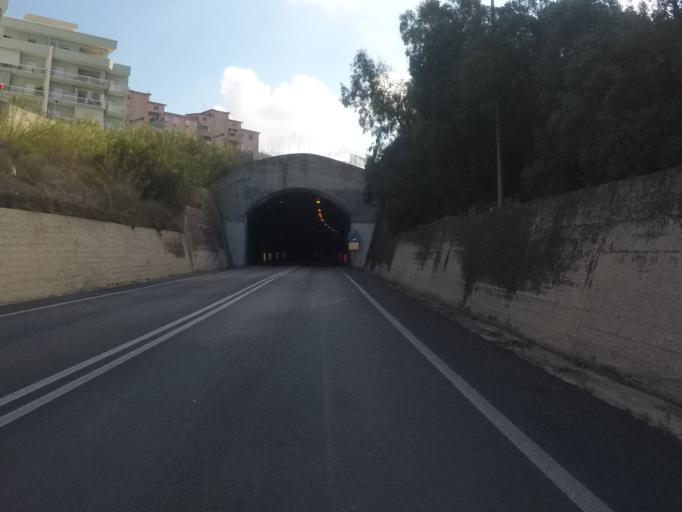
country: IT
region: Sicily
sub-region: Agrigento
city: Sciacca
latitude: 37.5187
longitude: 13.0807
